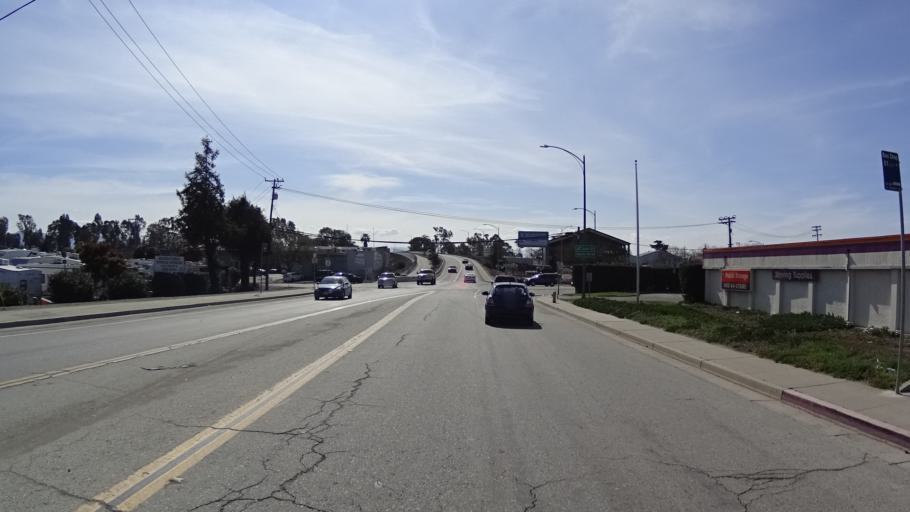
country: US
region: California
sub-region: Santa Clara County
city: San Jose
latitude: 37.3632
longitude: -121.8750
